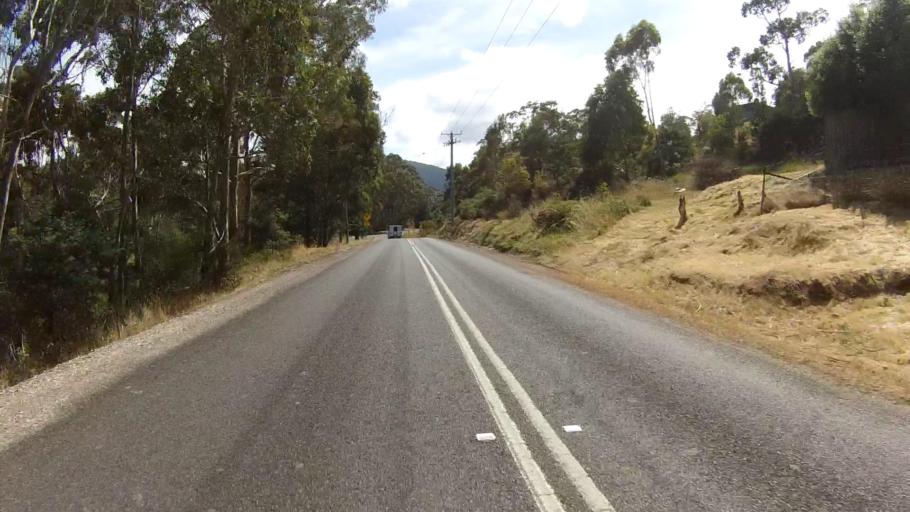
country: AU
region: Tasmania
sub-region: Huon Valley
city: Cygnet
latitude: -43.2429
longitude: 147.1510
